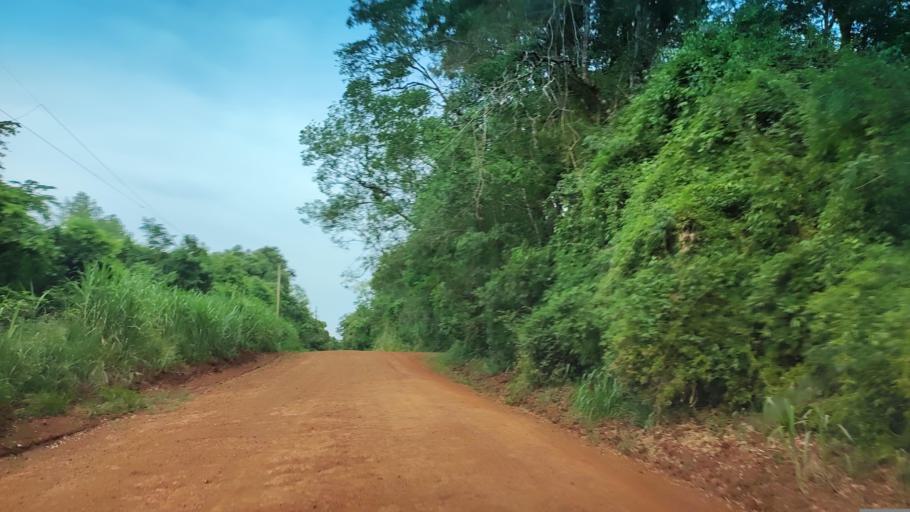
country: AR
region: Misiones
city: Gobernador Roca
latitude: -27.1470
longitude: -55.4785
